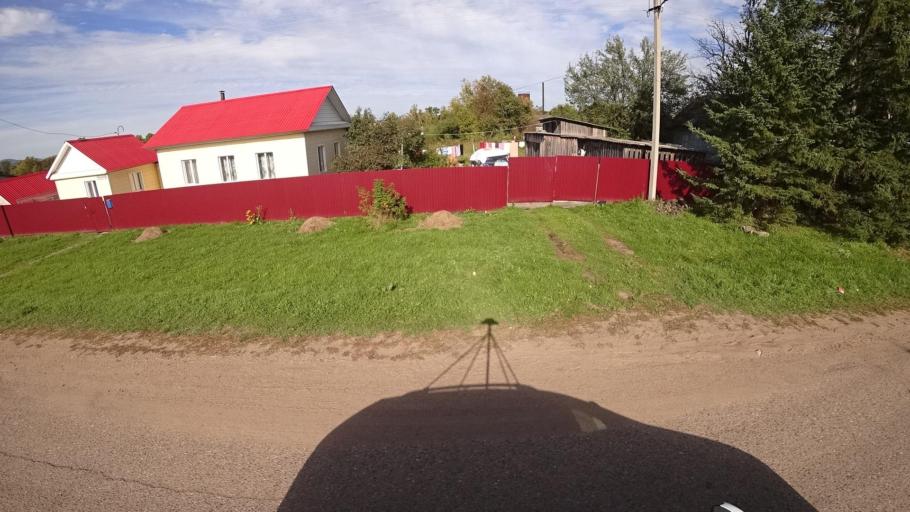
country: RU
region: Primorskiy
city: Dostoyevka
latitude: 44.2973
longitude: 133.4533
